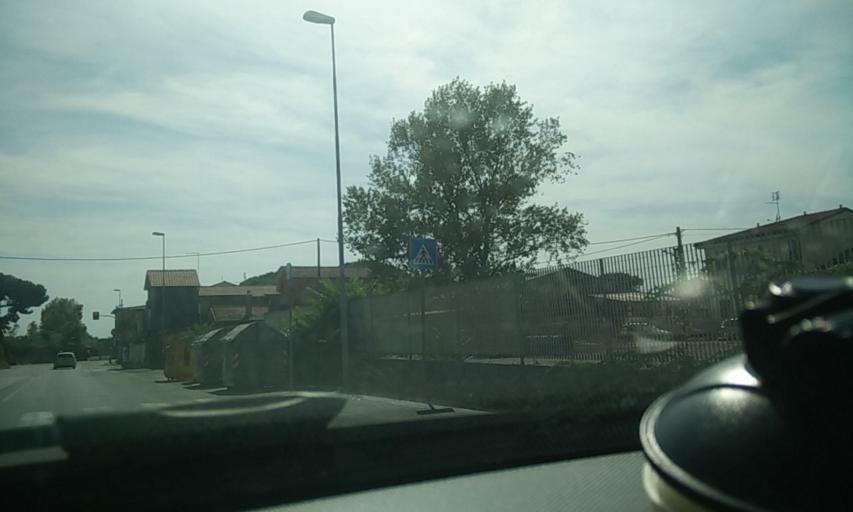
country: IT
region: Tuscany
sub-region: Provincia di Massa-Carrara
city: Carrara
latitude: 44.0512
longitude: 10.0746
